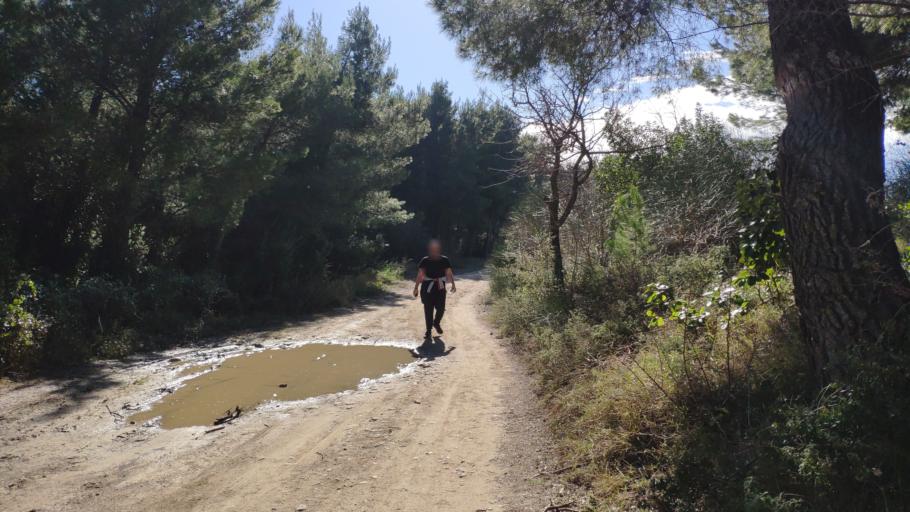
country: GR
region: Attica
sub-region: Nomarchia Anatolikis Attikis
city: Varybobi
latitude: 38.1544
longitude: 23.7766
